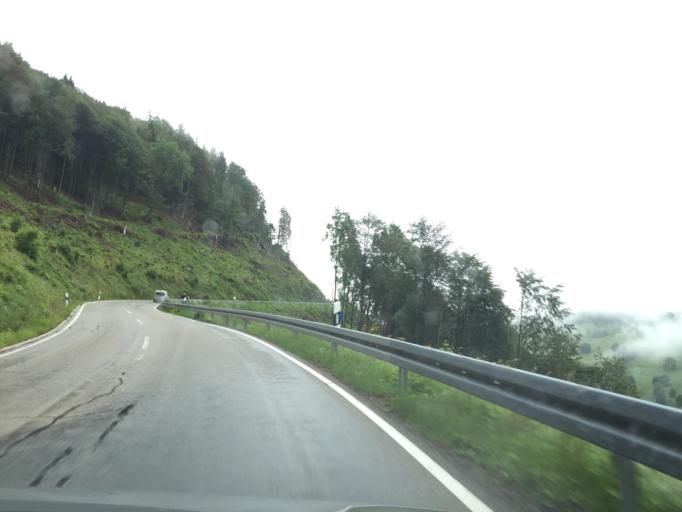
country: DE
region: Baden-Wuerttemberg
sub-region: Freiburg Region
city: Todtnau
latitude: 47.8495
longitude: 7.9249
